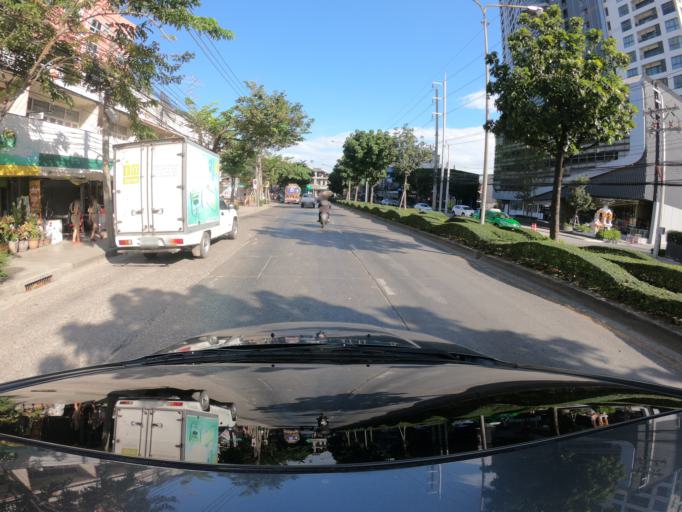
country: TH
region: Bangkok
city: Phra Khanong
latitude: 13.6737
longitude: 100.6042
